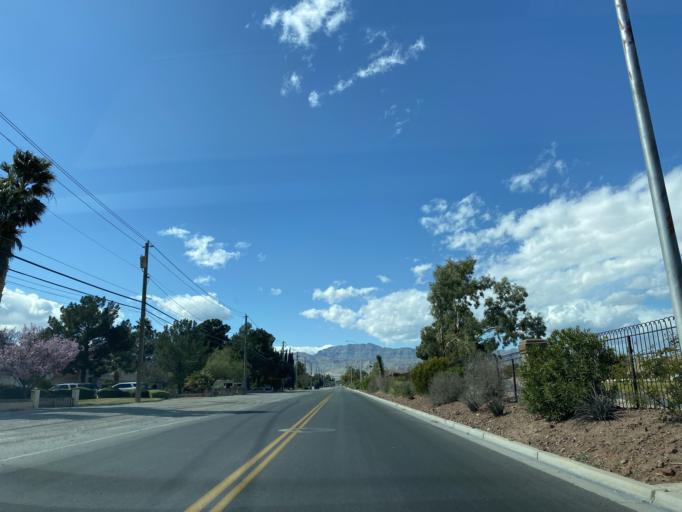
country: US
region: Nevada
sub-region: Clark County
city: Spring Valley
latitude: 36.2555
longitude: -115.2661
